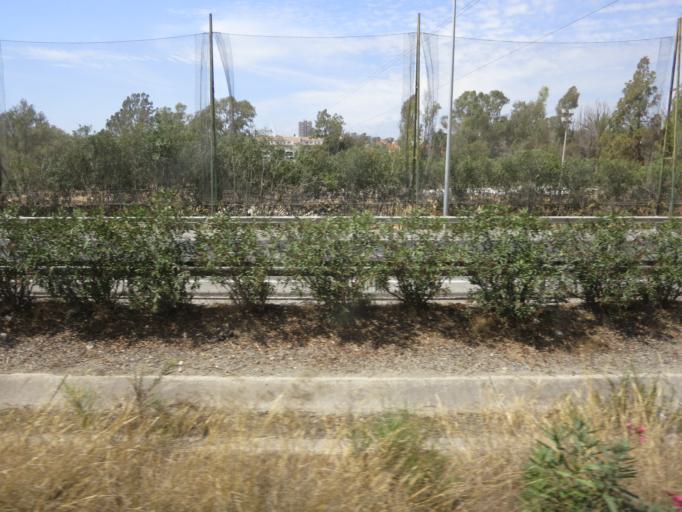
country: ES
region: Andalusia
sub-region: Provincia de Malaga
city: Marbella
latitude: 36.5034
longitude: -4.9473
